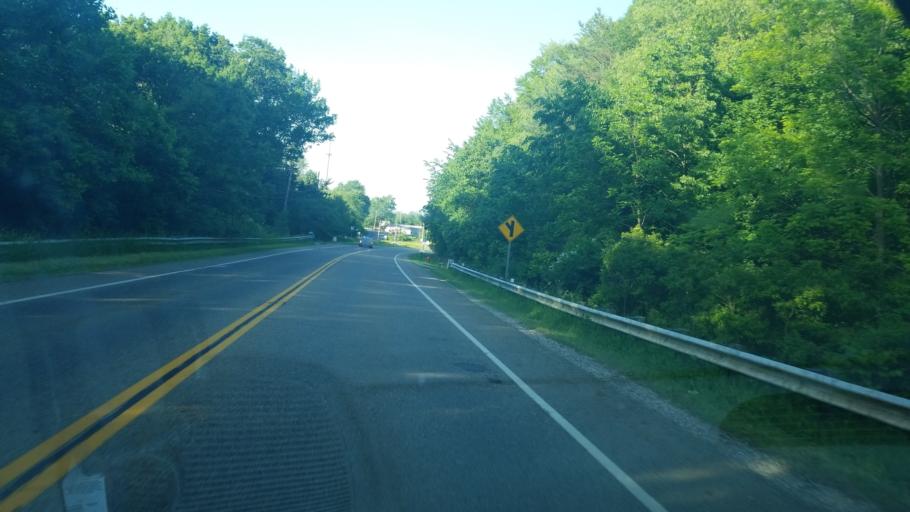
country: US
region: Ohio
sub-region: Portage County
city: Kent
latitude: 41.1334
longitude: -81.3953
